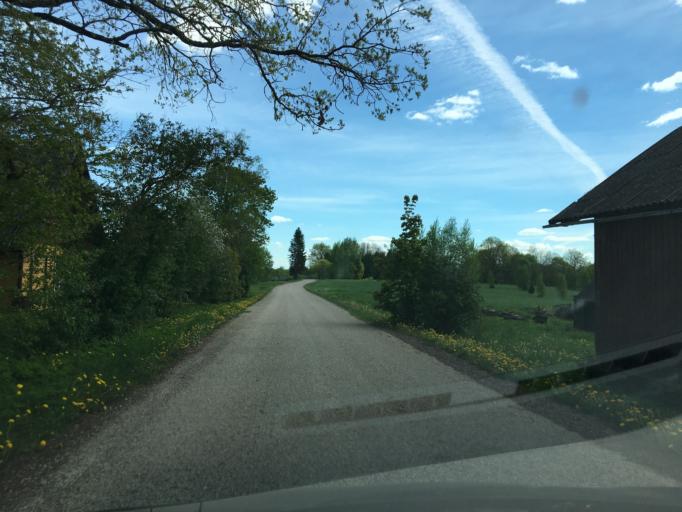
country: EE
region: Vorumaa
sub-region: Antsla vald
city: Vana-Antsla
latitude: 57.9150
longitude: 26.3278
